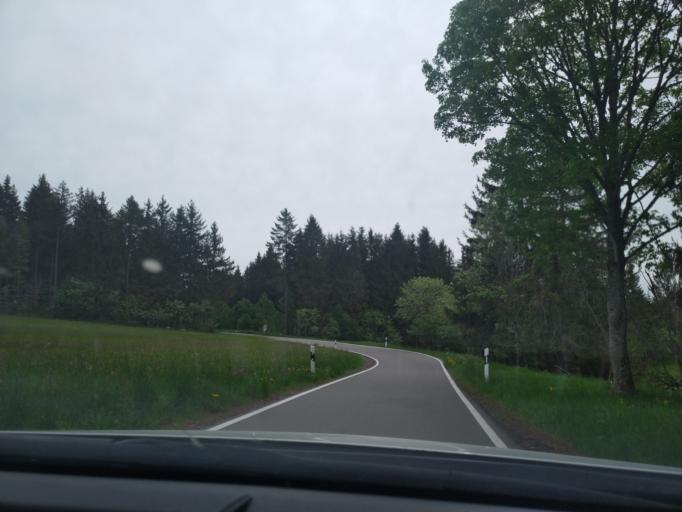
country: DE
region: Baden-Wuerttemberg
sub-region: Freiburg Region
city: Schluchsee
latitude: 47.8065
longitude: 8.2207
